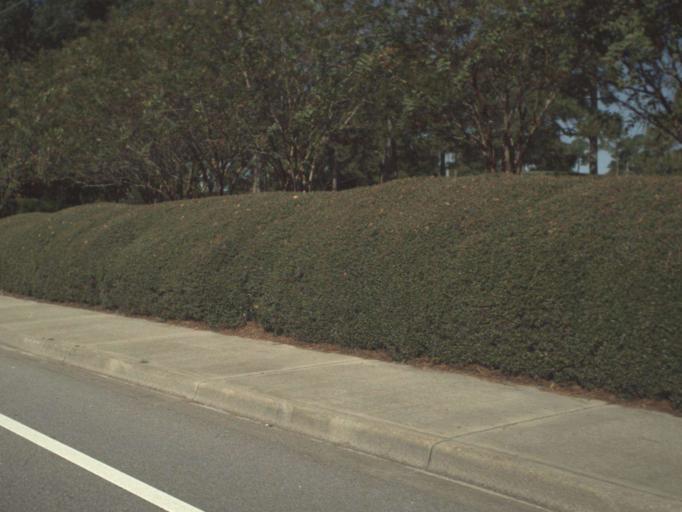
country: US
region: Florida
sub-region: Walton County
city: Miramar Beach
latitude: 30.3792
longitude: -86.3232
